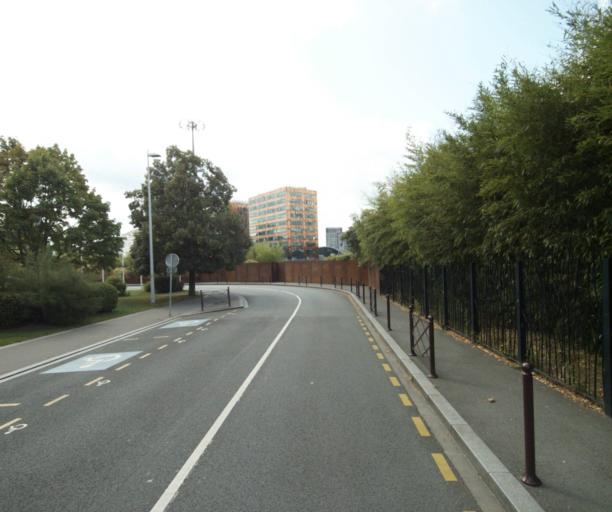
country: FR
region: Nord-Pas-de-Calais
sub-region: Departement du Nord
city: La Madeleine
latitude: 50.6422
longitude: 3.0753
